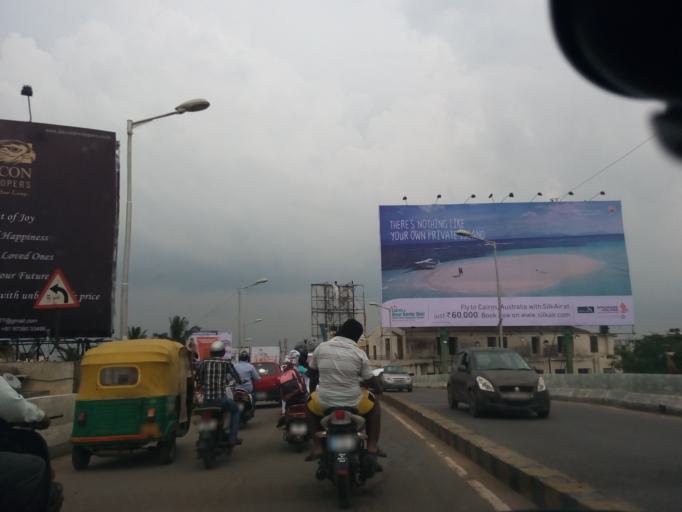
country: IN
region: Karnataka
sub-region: Bangalore Urban
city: Bangalore
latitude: 13.0086
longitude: 77.6229
